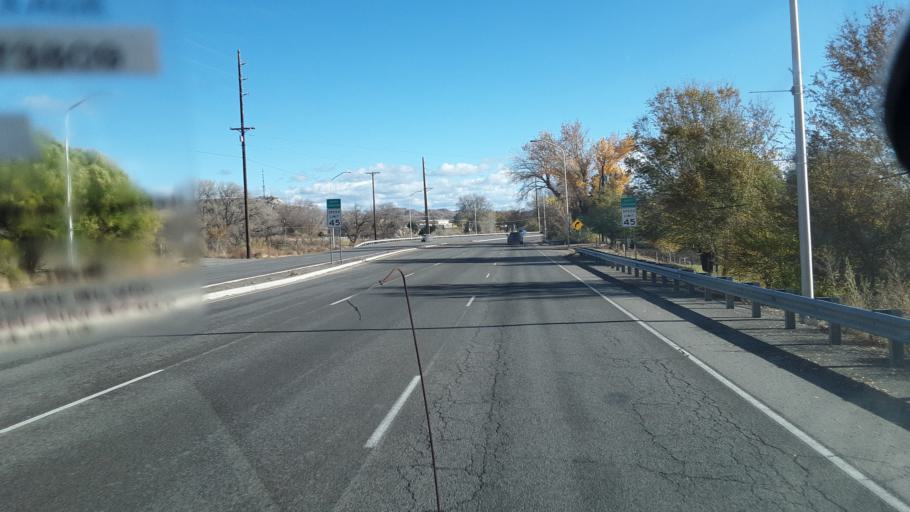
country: US
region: New Mexico
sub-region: San Juan County
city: Bloomfield
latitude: 36.7101
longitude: -108.0097
